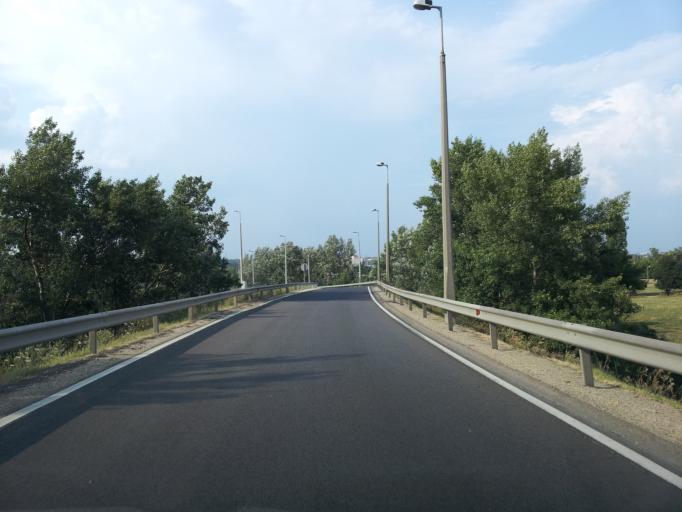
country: HU
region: Budapest
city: Budapest XXII. keruelet
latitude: 47.3981
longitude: 19.0119
